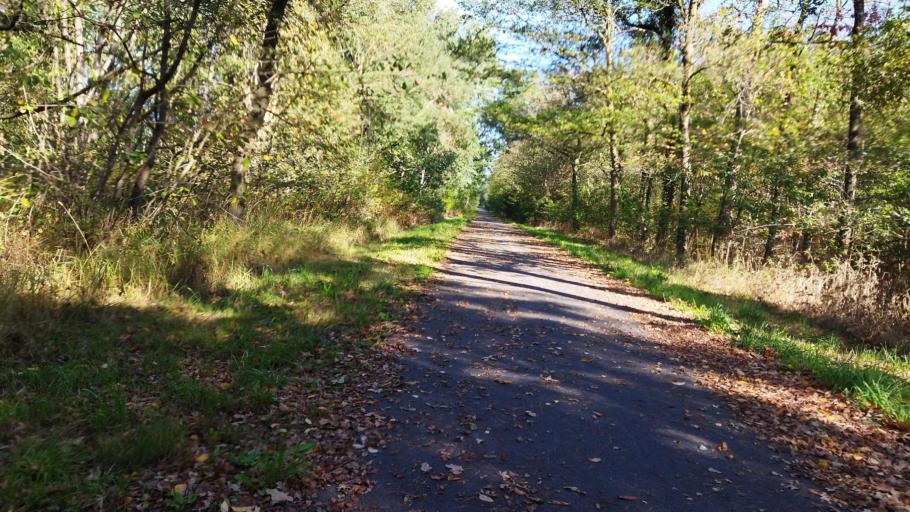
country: DE
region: Lower Saxony
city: Ohne
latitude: 52.2659
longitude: 7.3138
